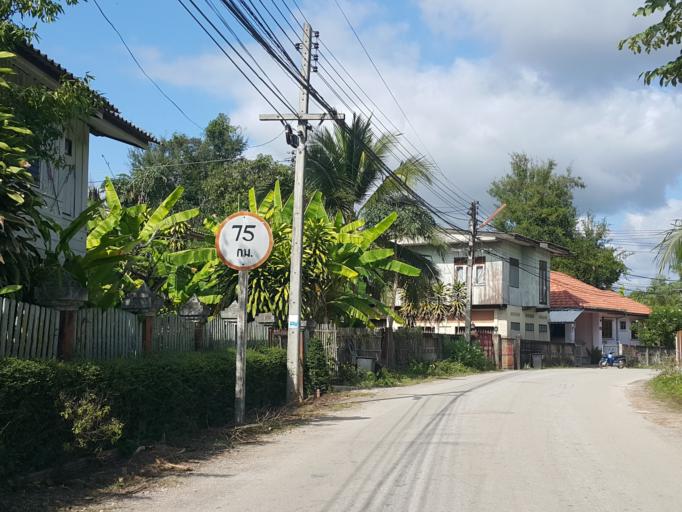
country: TH
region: Lampang
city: Hang Chat
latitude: 18.3387
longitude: 99.3571
